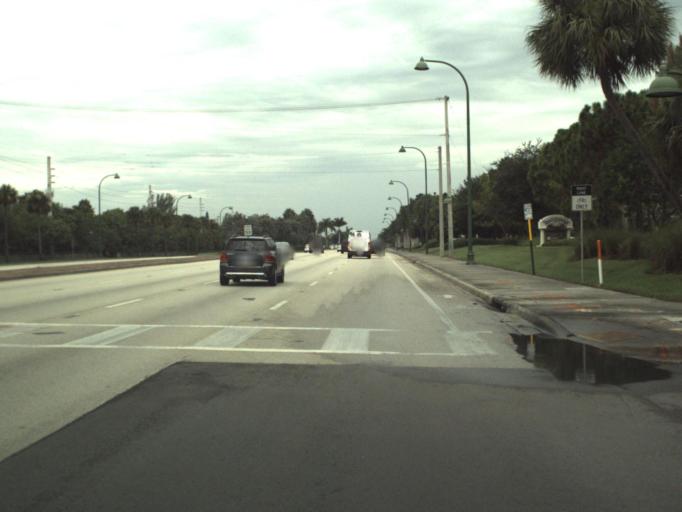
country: US
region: Florida
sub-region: Palm Beach County
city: Royal Palm Beach
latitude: 26.6811
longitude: -80.2196
